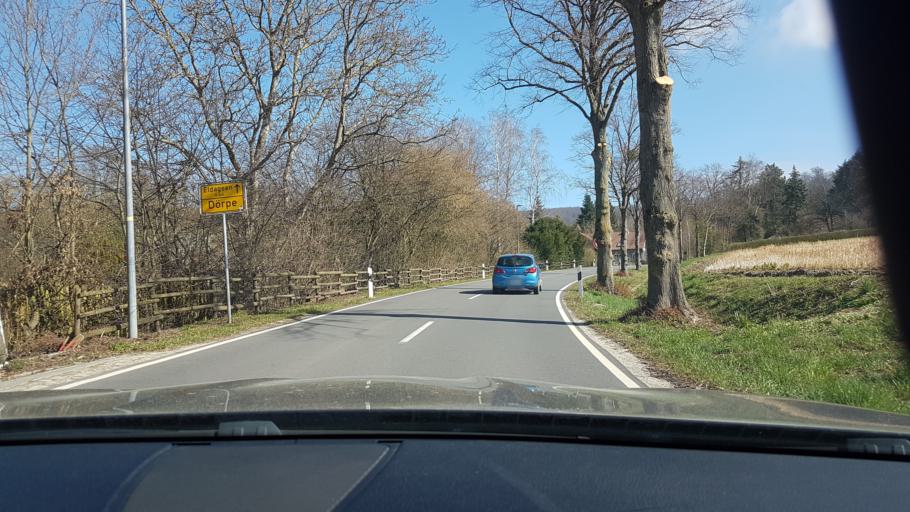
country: DE
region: Lower Saxony
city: Coppenbrugge
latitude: 52.1389
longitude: 9.5691
